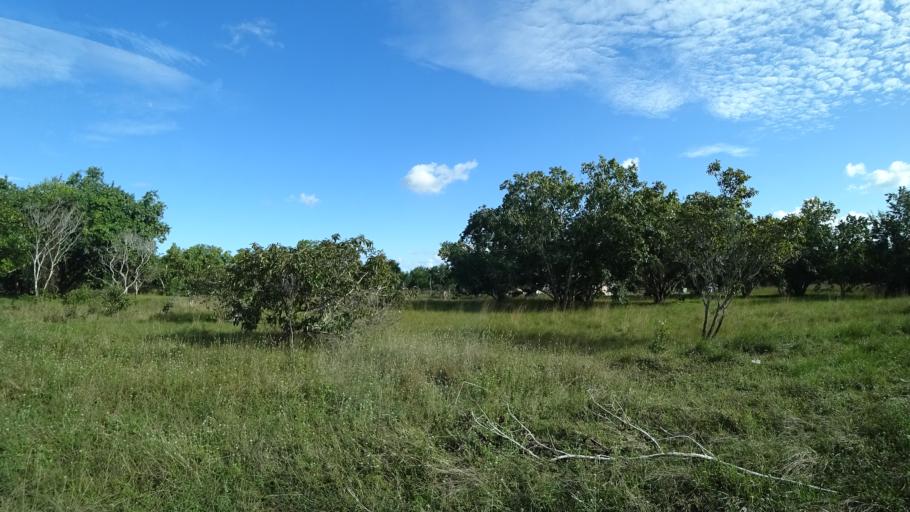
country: BZ
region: Belize
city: Belize City
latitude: 17.5576
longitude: -88.3994
